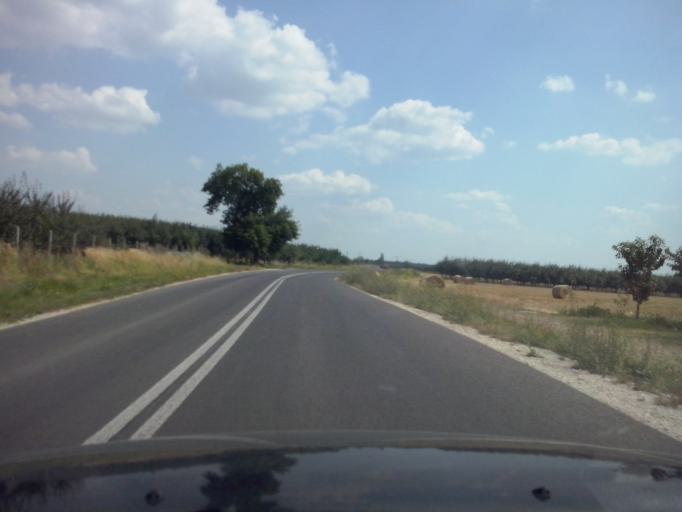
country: PL
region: Swietokrzyskie
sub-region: Powiat staszowski
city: Szydlow
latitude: 50.5865
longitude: 21.0341
